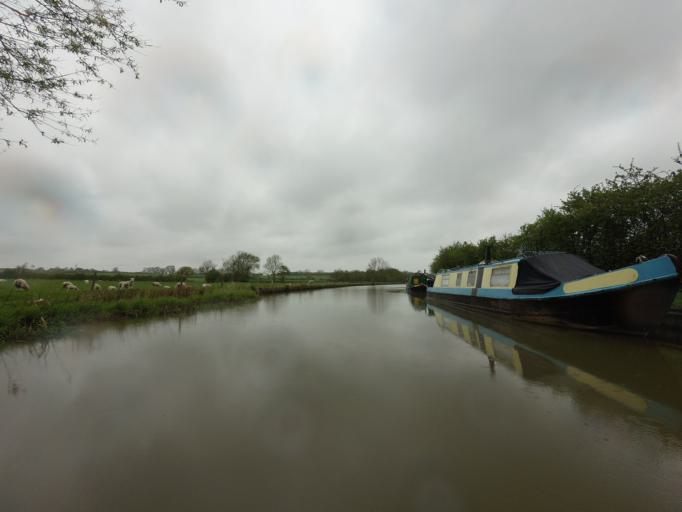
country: GB
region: England
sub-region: Northamptonshire
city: Roade
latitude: 52.1189
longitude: -0.8900
